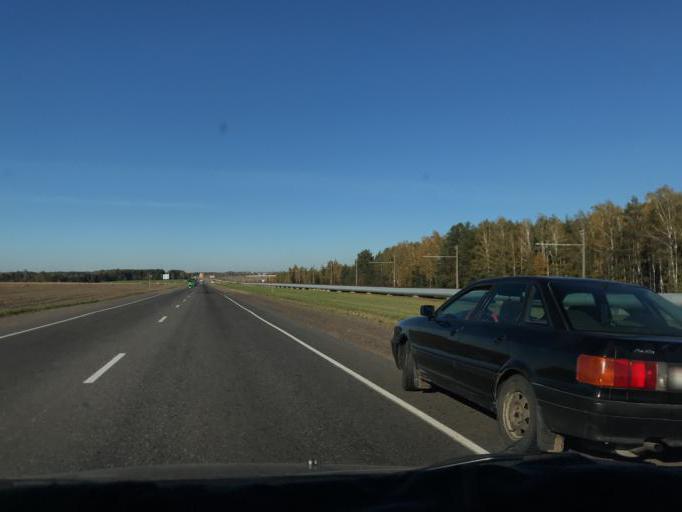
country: BY
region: Gomel
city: Mazyr
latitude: 51.9819
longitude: 29.2600
